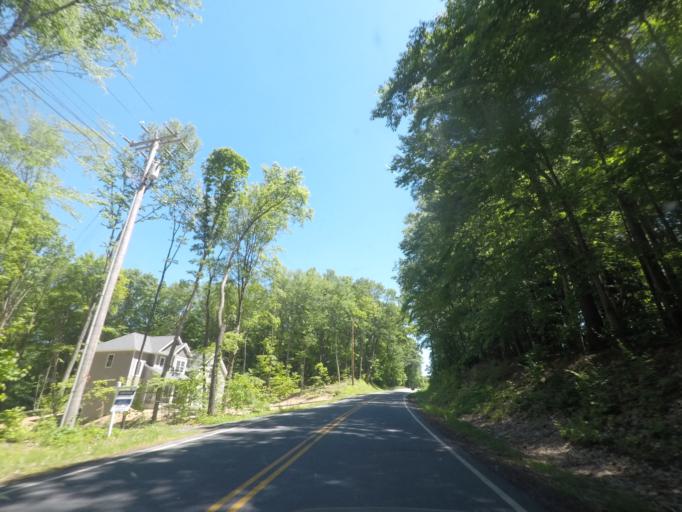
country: US
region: New York
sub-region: Saratoga County
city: Country Knolls
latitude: 42.9438
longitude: -73.7604
